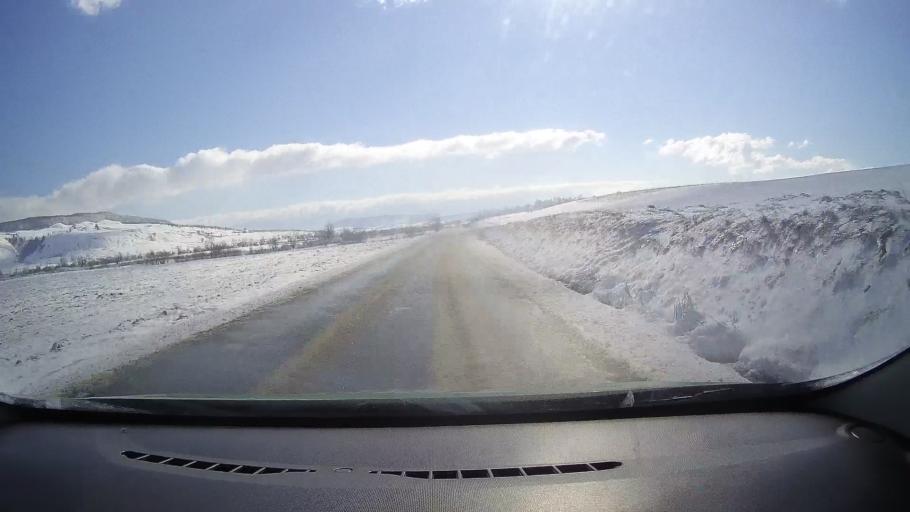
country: RO
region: Sibiu
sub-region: Comuna Rosia
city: Rosia
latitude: 45.8289
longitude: 24.3129
